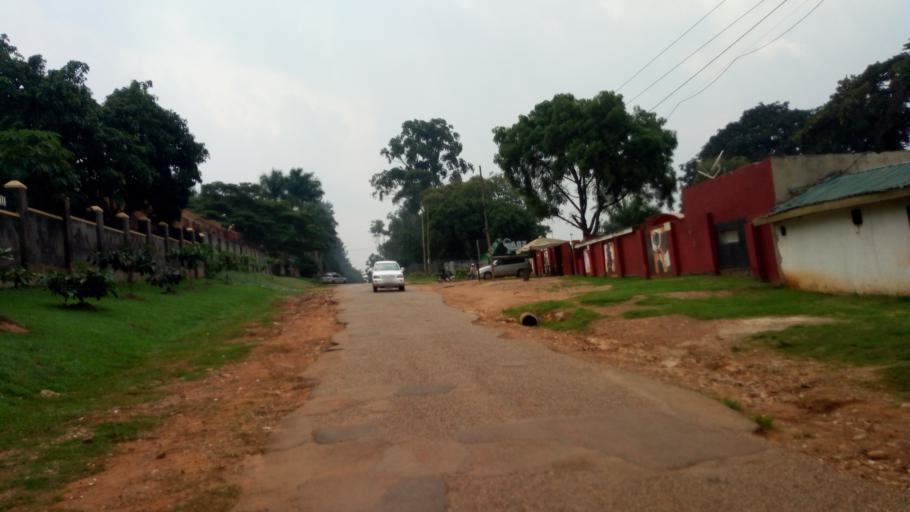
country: UG
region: Central Region
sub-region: Kampala District
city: Kampala
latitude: 0.3107
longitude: 32.6254
